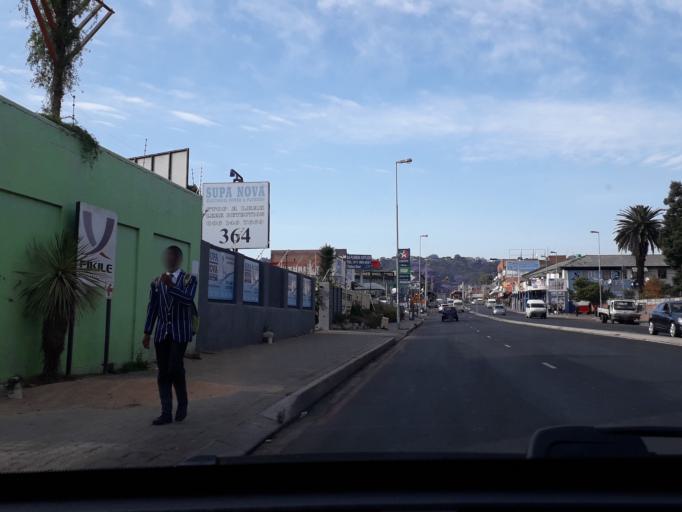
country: ZA
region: Gauteng
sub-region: City of Johannesburg Metropolitan Municipality
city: Johannesburg
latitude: -26.1549
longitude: 28.0858
